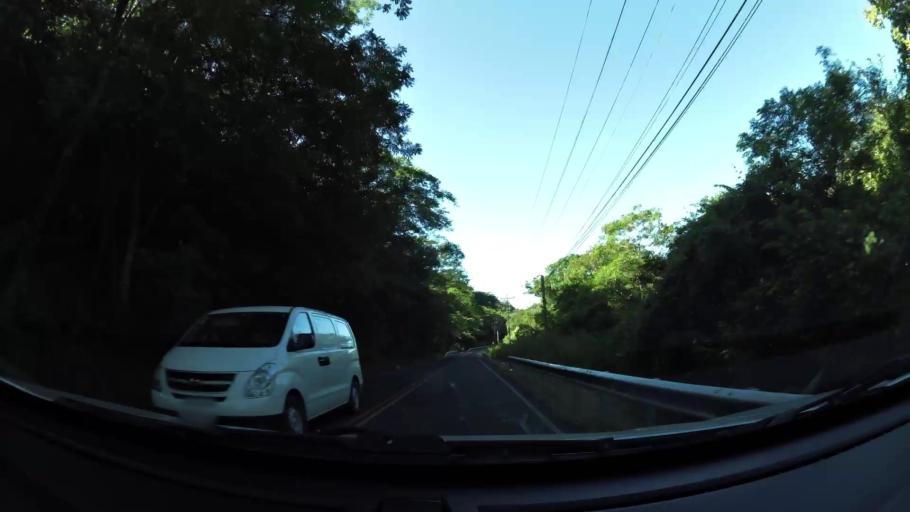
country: CR
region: Guanacaste
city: Belen
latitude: 10.3764
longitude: -85.6231
